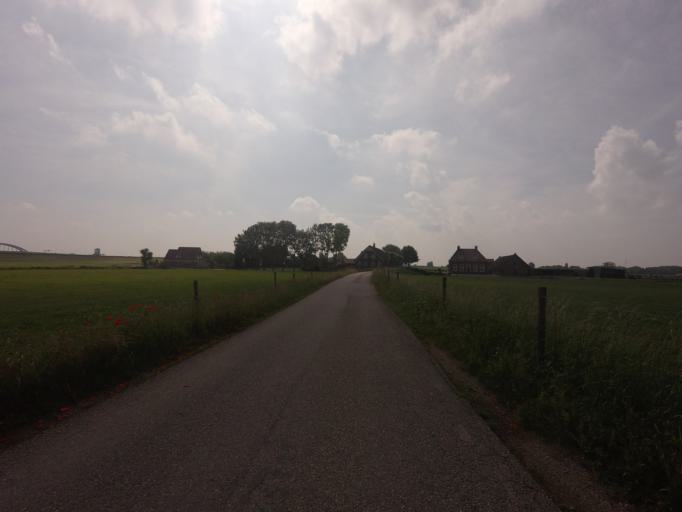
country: NL
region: Utrecht
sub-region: Gemeente IJsselstein
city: IJsselstein
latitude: 51.9999
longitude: 5.0606
